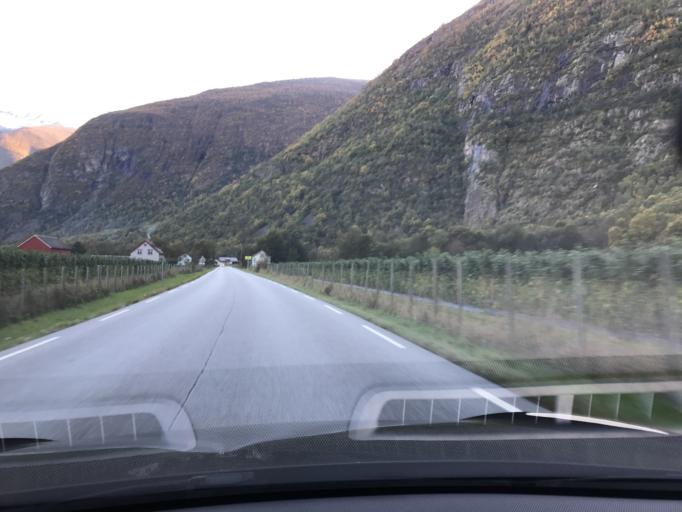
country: NO
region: Sogn og Fjordane
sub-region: Laerdal
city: Laerdalsoyri
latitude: 61.0737
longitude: 7.5006
